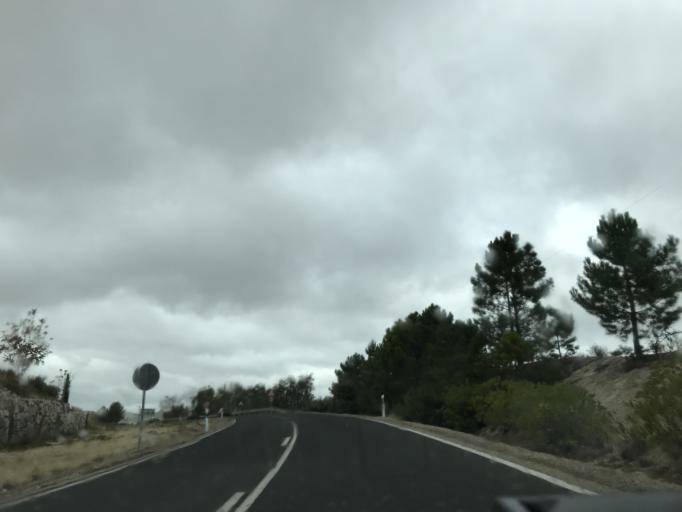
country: ES
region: Andalusia
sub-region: Provincia de Jaen
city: Peal de Becerro
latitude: 37.9196
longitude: -3.1183
